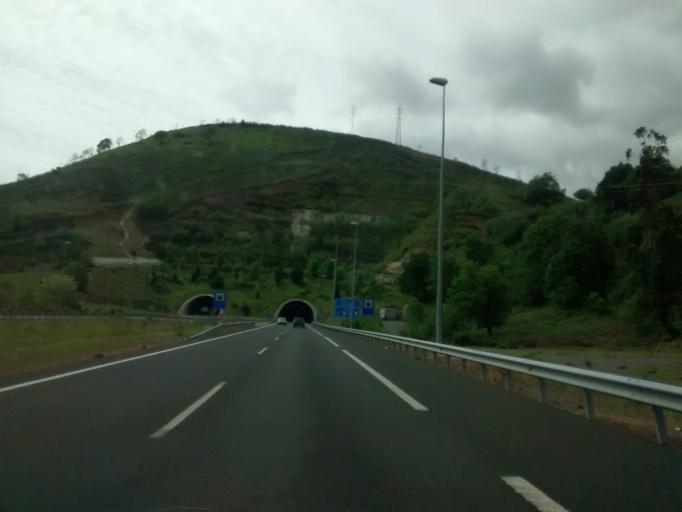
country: ES
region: Cantabria
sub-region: Provincia de Cantabria
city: Arenas de Iguna
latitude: 43.2150
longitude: -4.0783
